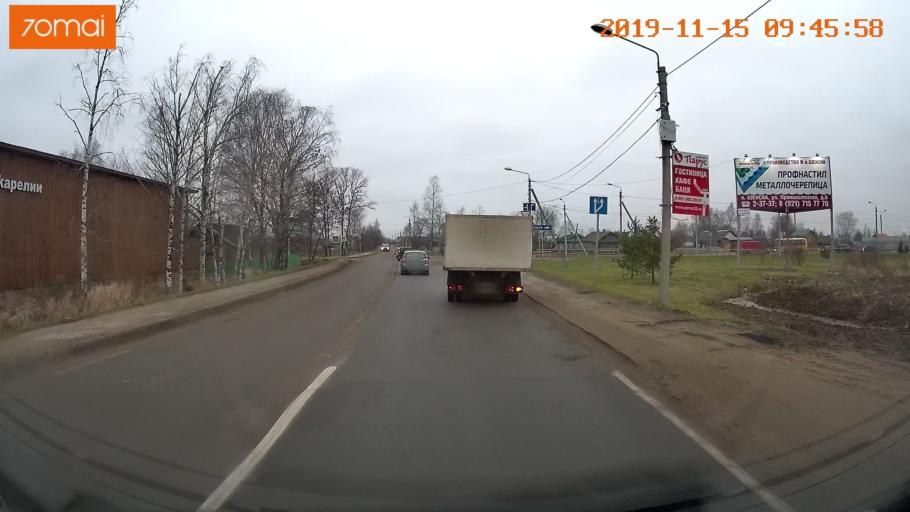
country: RU
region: Vologda
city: Sheksna
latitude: 59.2111
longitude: 38.5123
